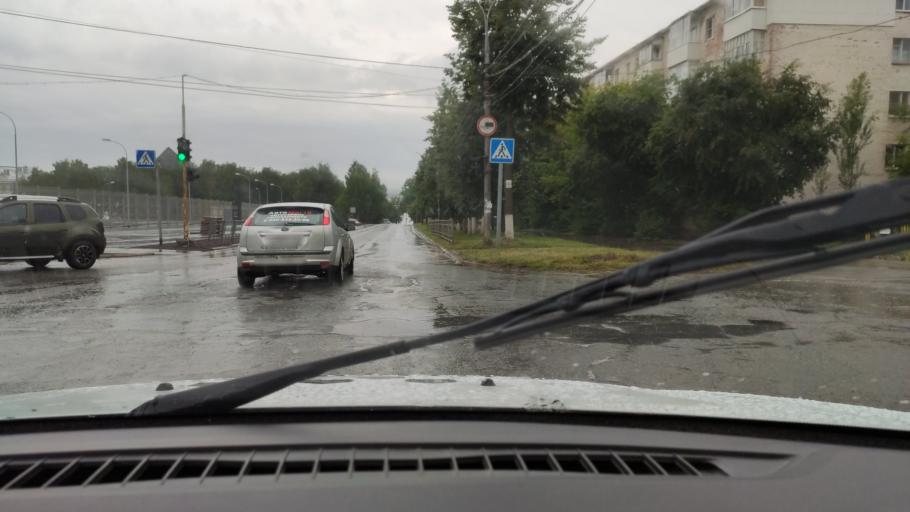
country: RU
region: Udmurtiya
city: Votkinsk
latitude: 57.0621
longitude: 53.9927
